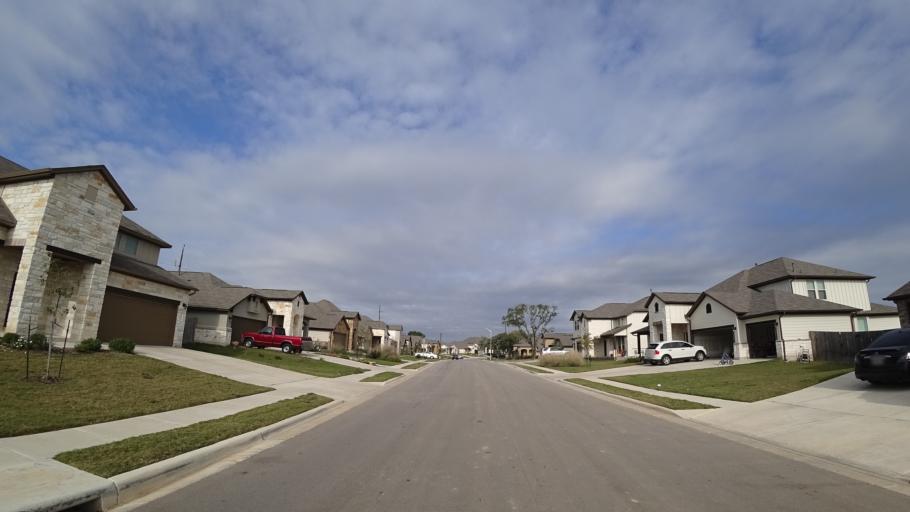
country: US
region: Texas
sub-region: Travis County
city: Manchaca
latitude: 30.1300
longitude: -97.8479
